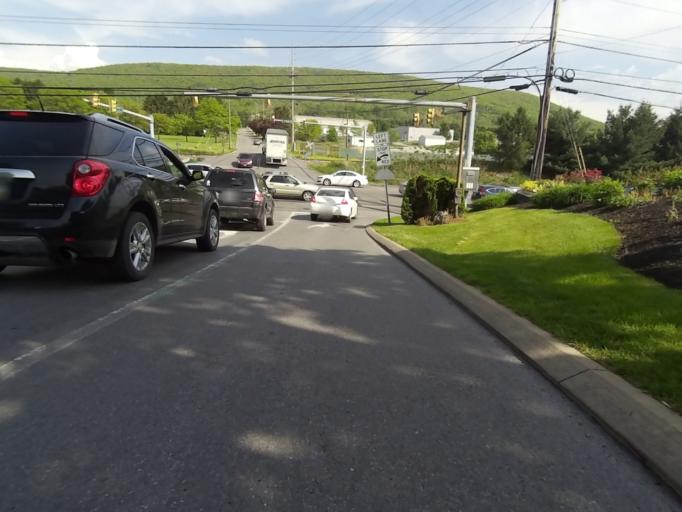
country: US
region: Pennsylvania
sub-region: Centre County
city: Lemont
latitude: 40.8266
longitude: -77.8092
